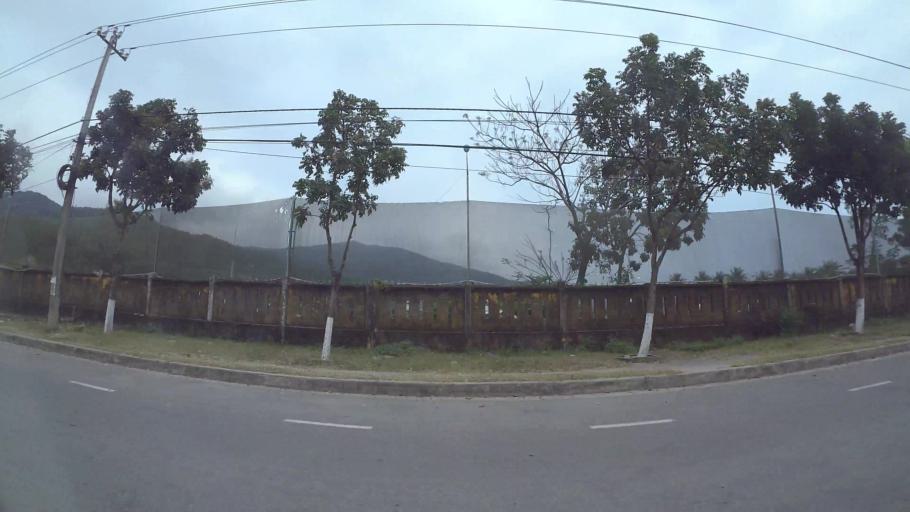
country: VN
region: Da Nang
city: Da Nang
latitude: 16.1039
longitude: 108.2472
